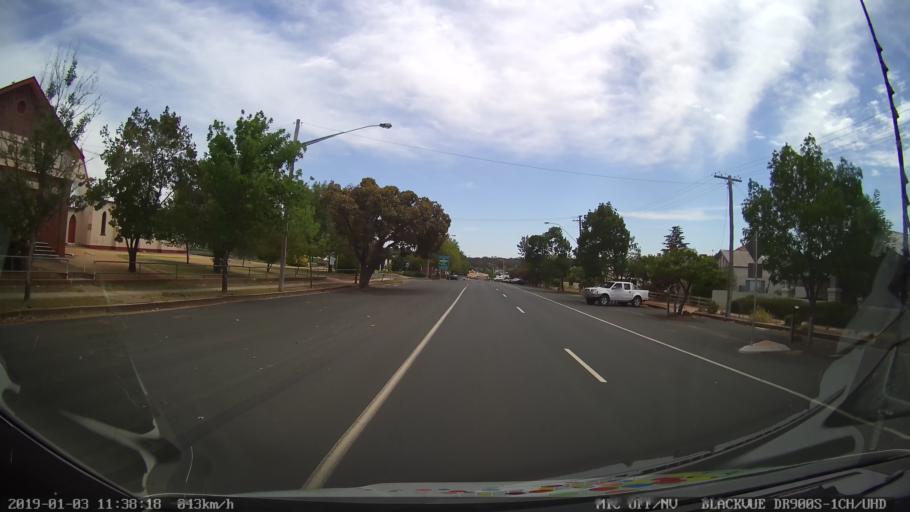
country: AU
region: New South Wales
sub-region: Weddin
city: Grenfell
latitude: -33.8972
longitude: 148.1623
